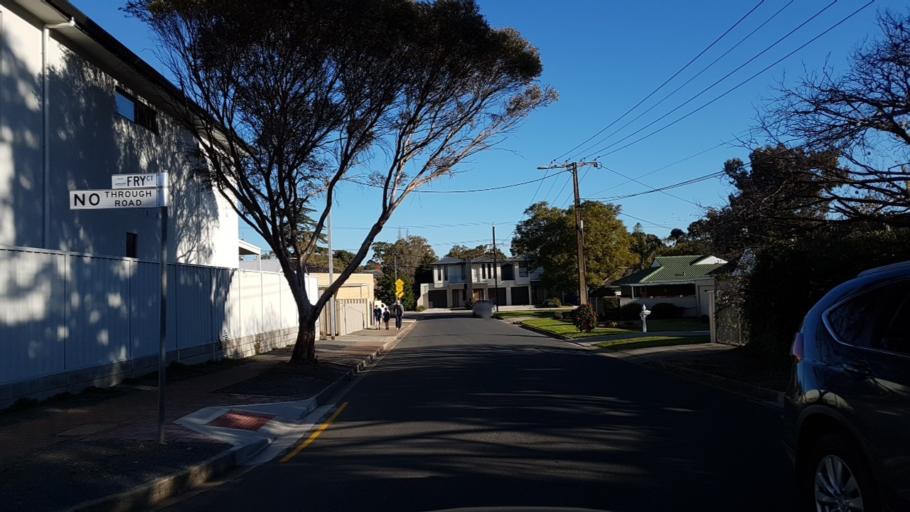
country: AU
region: South Australia
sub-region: Campbelltown
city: Campbelltown
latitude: -34.8821
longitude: 138.6585
